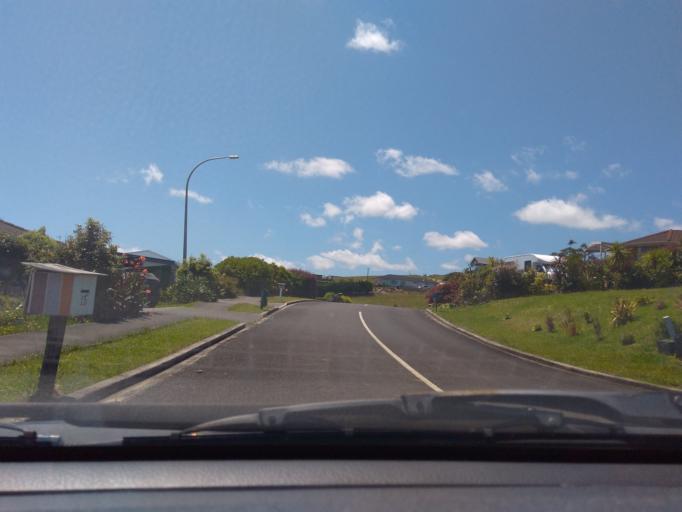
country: NZ
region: Northland
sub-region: Far North District
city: Taipa
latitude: -34.9939
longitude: 173.5079
